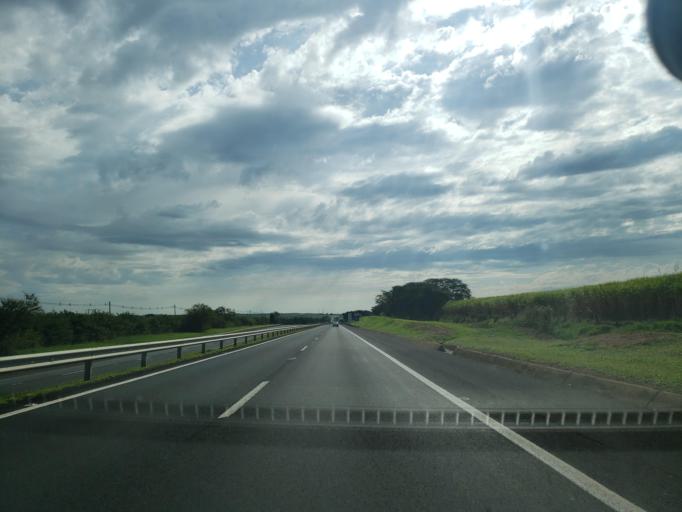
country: BR
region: Sao Paulo
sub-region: Cafelandia
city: Cafelandia
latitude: -21.8694
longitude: -49.5681
